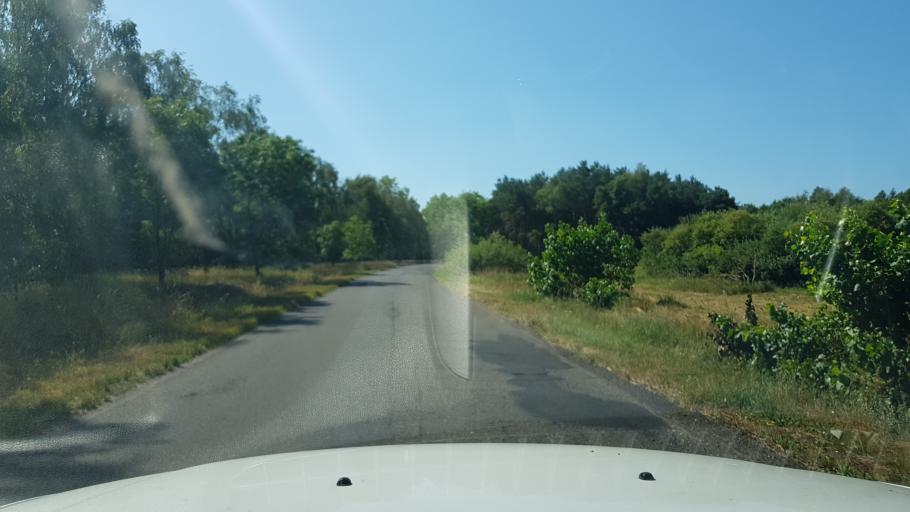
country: PL
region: West Pomeranian Voivodeship
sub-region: Powiat goleniowski
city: Goleniow
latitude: 53.4687
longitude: 14.7152
